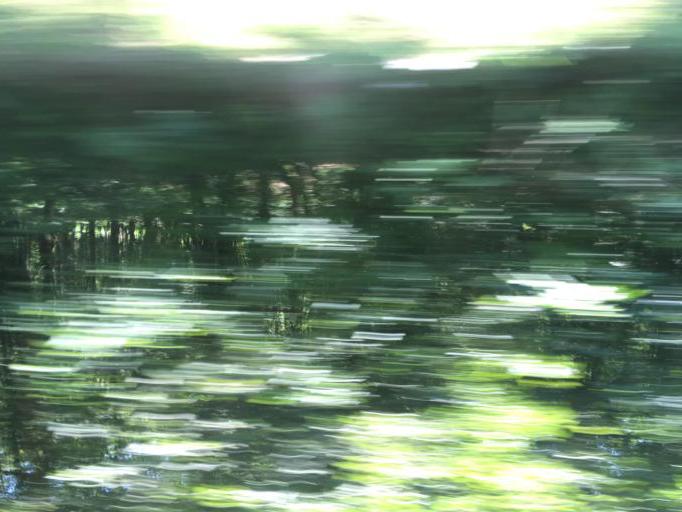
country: SI
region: Metlika
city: Metlika
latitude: 45.5910
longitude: 15.3440
